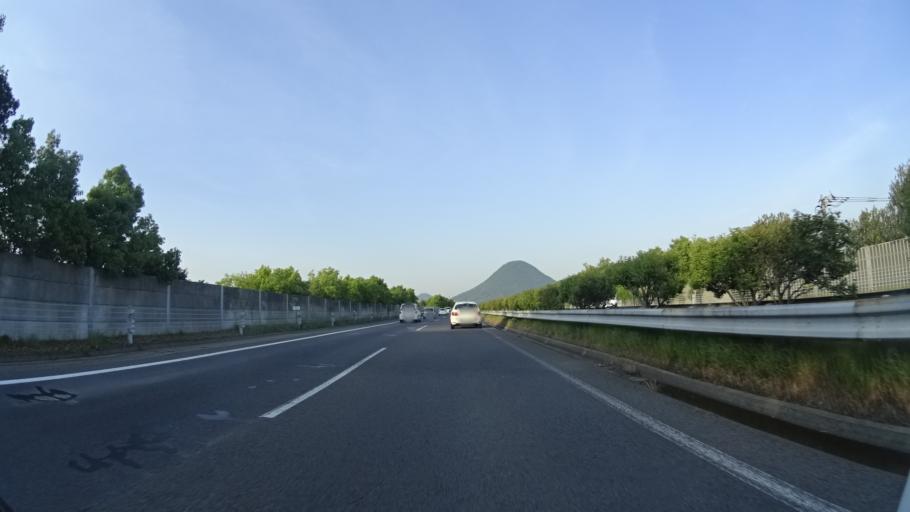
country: JP
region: Kagawa
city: Marugame
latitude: 34.2567
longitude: 133.8072
